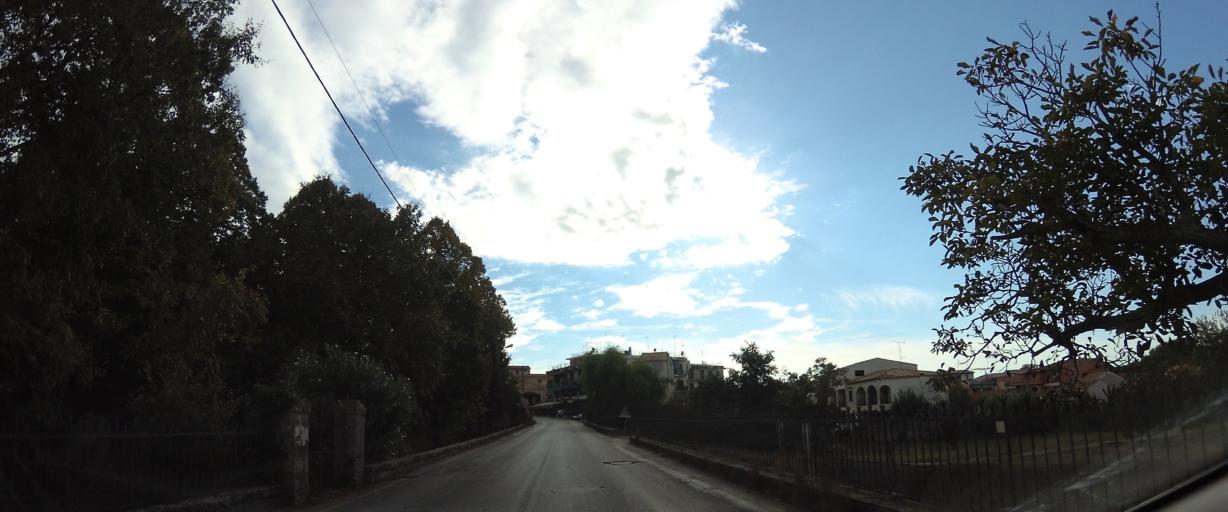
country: GR
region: Ionian Islands
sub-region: Nomos Kerkyras
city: Kerkyra
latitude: 39.6072
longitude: 19.9223
